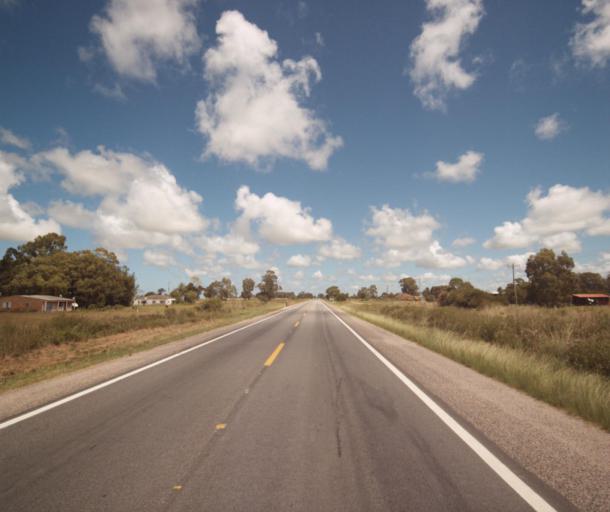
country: UY
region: Cerro Largo
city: Rio Branco
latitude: -32.9734
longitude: -52.7977
